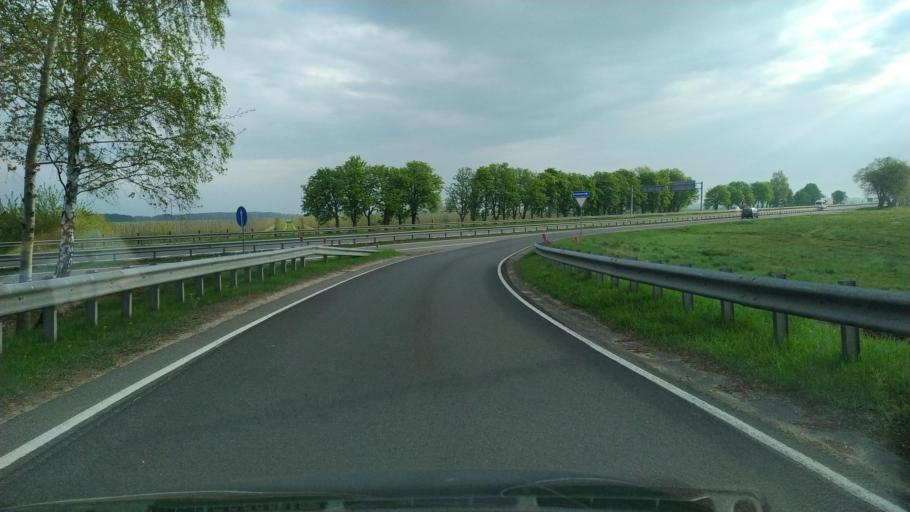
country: BY
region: Brest
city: Zhabinka
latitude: 52.1561
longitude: 24.0578
